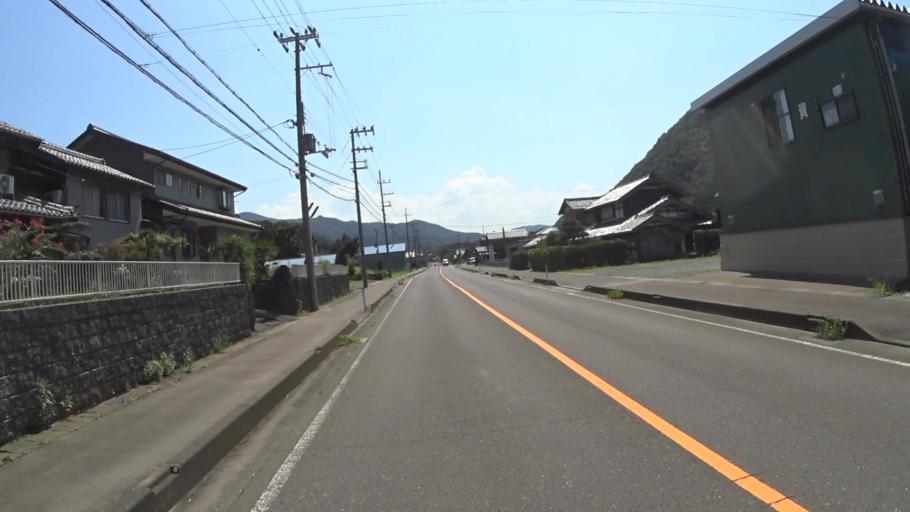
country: JP
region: Fukui
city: Obama
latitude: 35.4664
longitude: 135.7296
